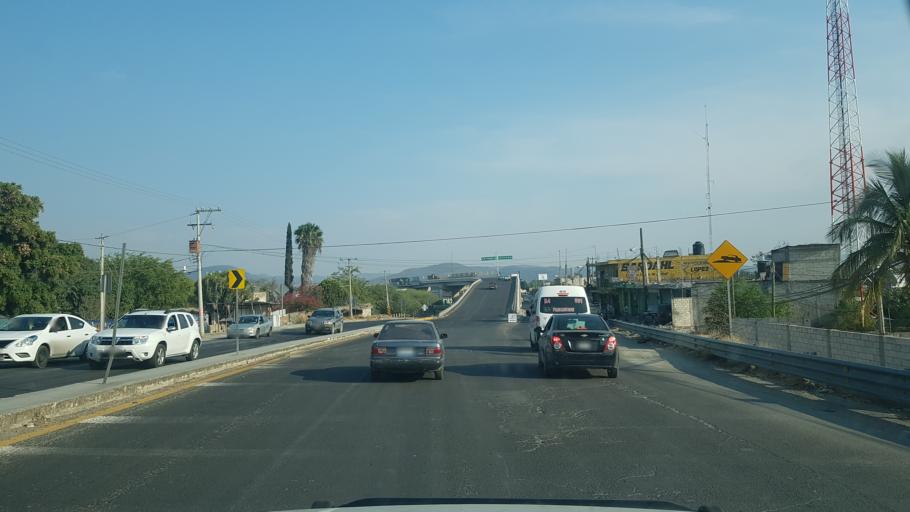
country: MX
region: Puebla
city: Izucar de Matamoros
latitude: 18.6020
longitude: -98.4817
